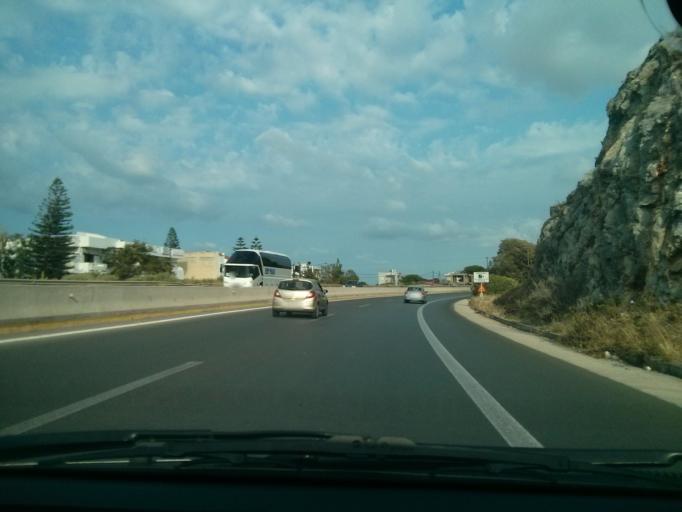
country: GR
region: Crete
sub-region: Nomos Irakleiou
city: Kokkini Hani
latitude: 35.3303
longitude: 25.2425
